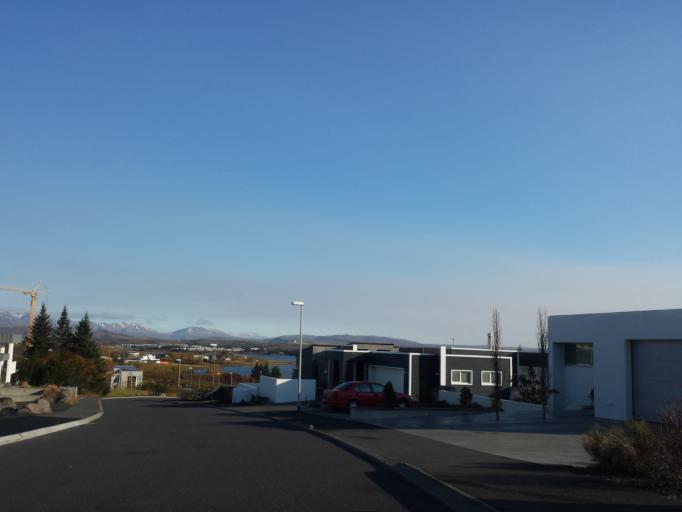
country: IS
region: Capital Region
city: Reykjavik
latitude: 64.0814
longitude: -21.8114
